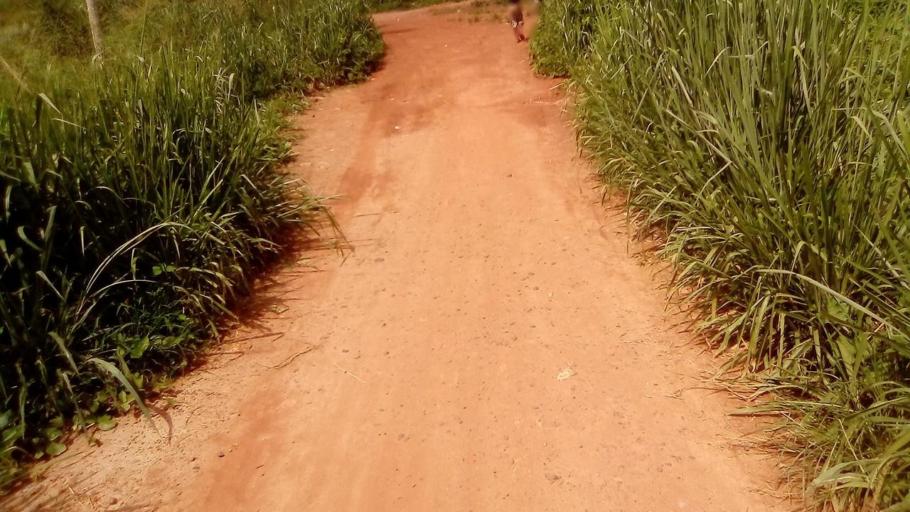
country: SL
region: Southern Province
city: Bo
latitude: 7.9668
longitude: -11.7196
